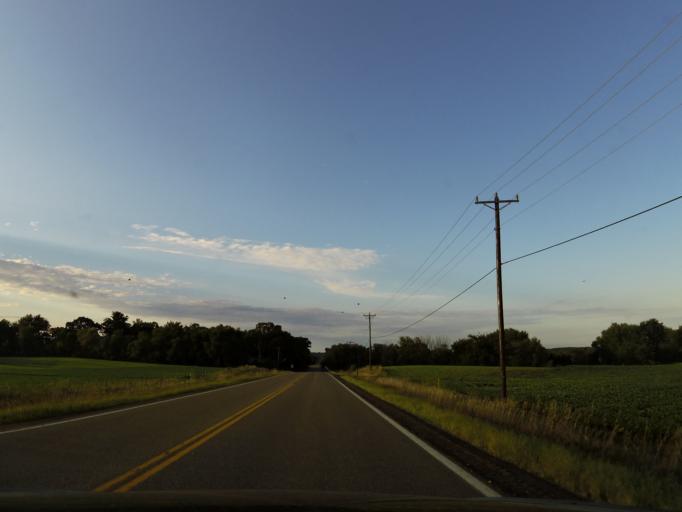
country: US
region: Minnesota
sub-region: Washington County
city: Afton
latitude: 44.9254
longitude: -92.8428
